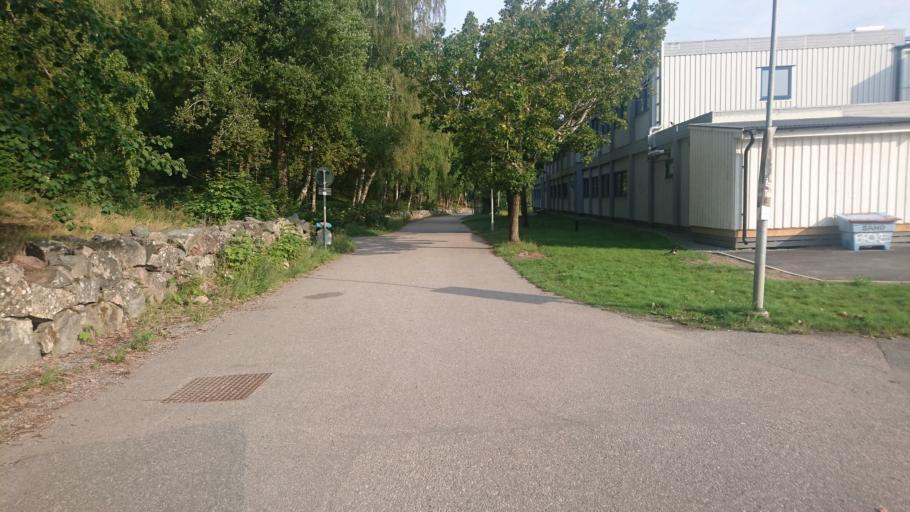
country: SE
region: Stockholm
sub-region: Upplands Vasby Kommun
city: Upplands Vaesby
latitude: 59.5109
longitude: 17.9146
